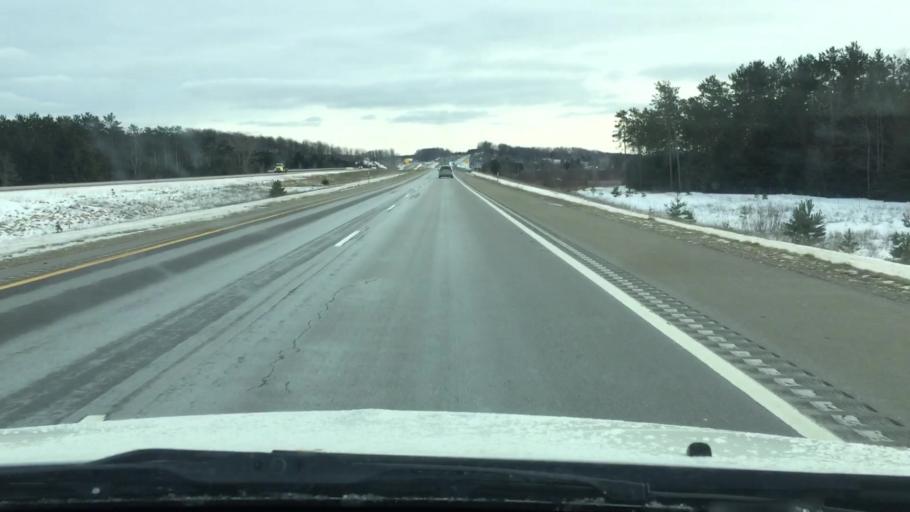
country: US
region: Michigan
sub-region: Wexford County
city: Manton
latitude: 44.4326
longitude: -85.3914
